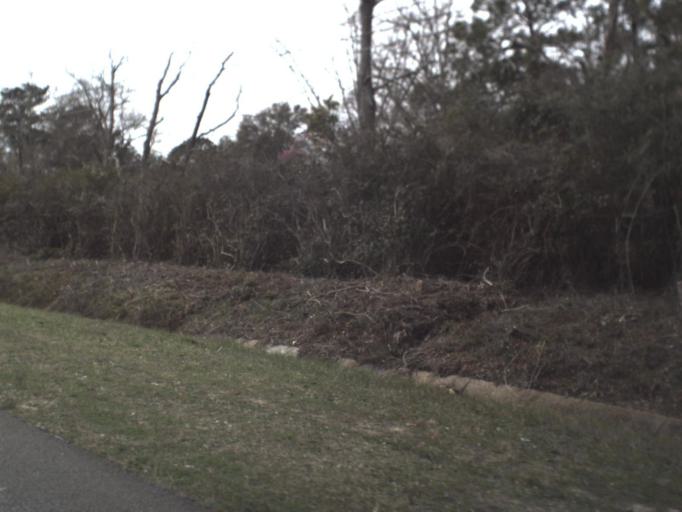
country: US
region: Florida
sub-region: Bay County
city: Hiland Park
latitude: 30.2277
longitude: -85.5871
